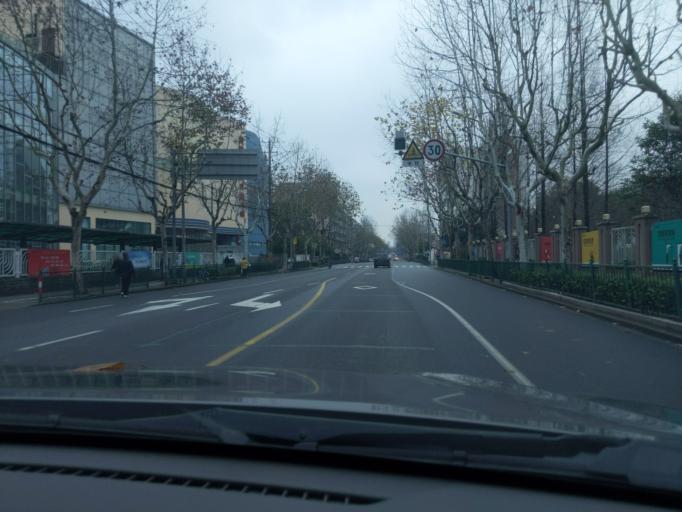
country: CN
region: Shanghai Shi
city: Huamu
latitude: 31.1829
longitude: 121.5050
